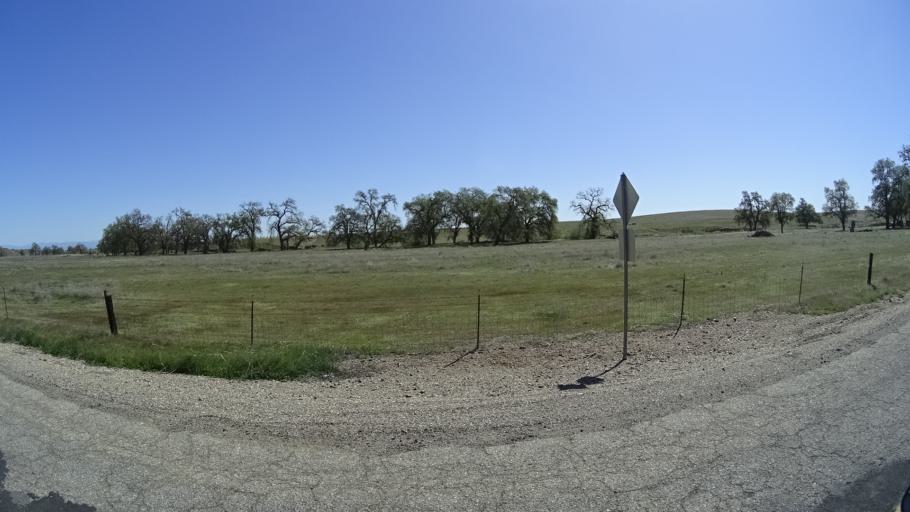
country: US
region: California
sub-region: Glenn County
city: Orland
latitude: 39.7722
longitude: -122.3227
